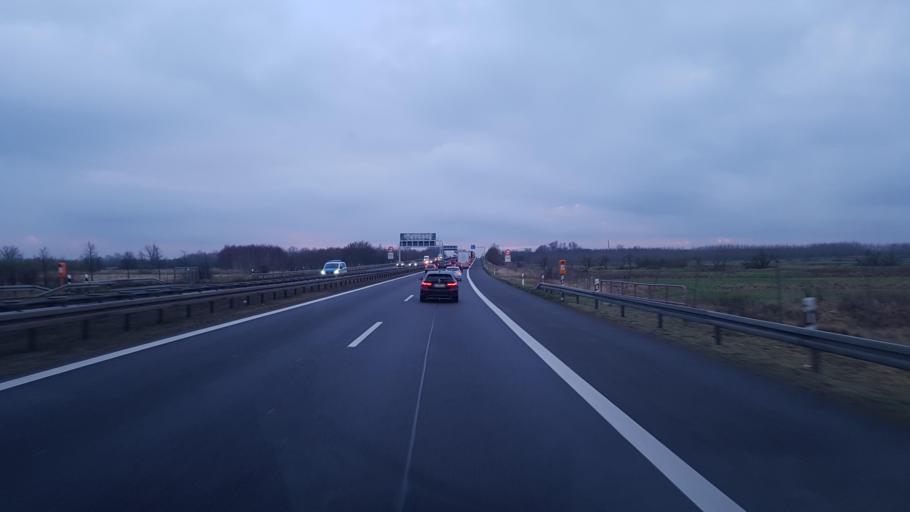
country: DE
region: Brandenburg
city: Mittenwalde
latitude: 52.3079
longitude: 13.5532
